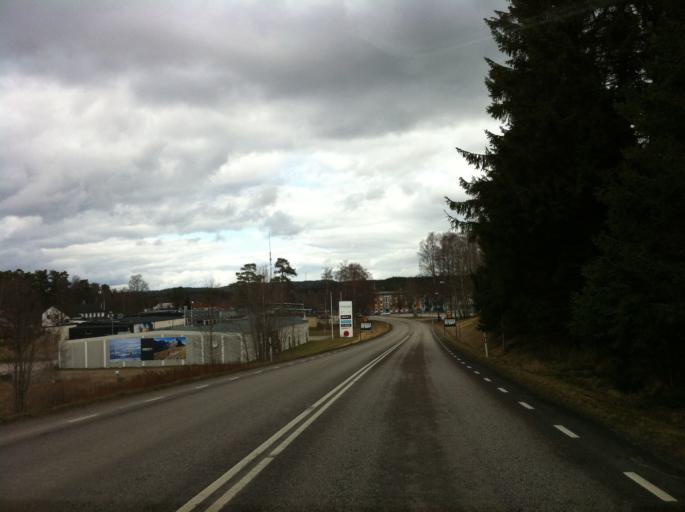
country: SE
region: Vaestra Goetaland
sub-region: Tranemo Kommun
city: Limmared
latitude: 57.6375
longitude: 13.4451
